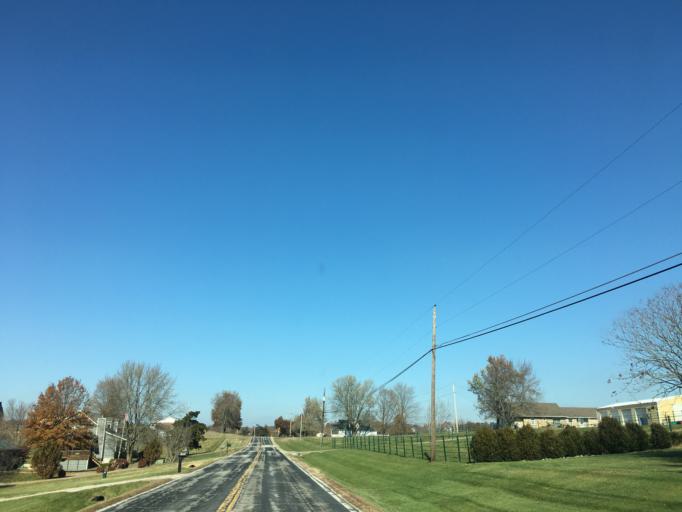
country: US
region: Missouri
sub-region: Cole County
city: Wardsville
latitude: 38.4719
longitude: -92.1775
